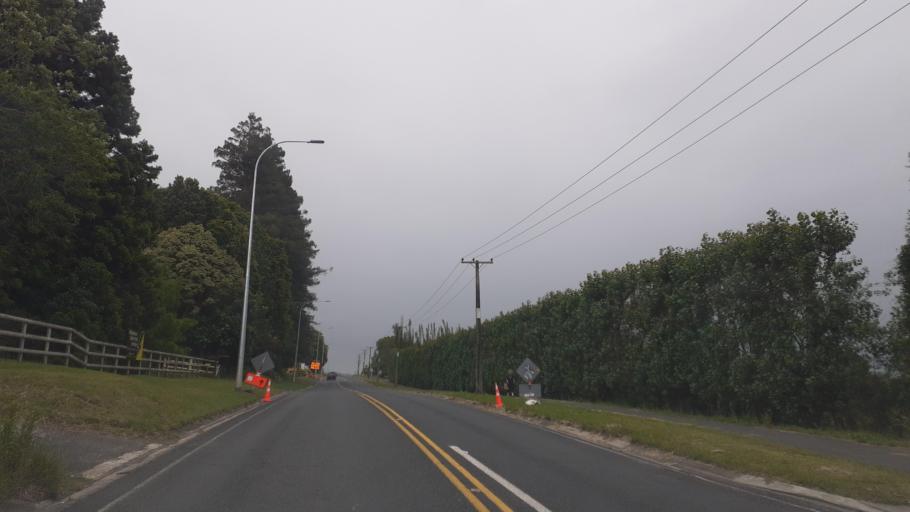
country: NZ
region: Northland
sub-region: Far North District
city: Kerikeri
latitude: -35.2396
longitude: 173.9384
